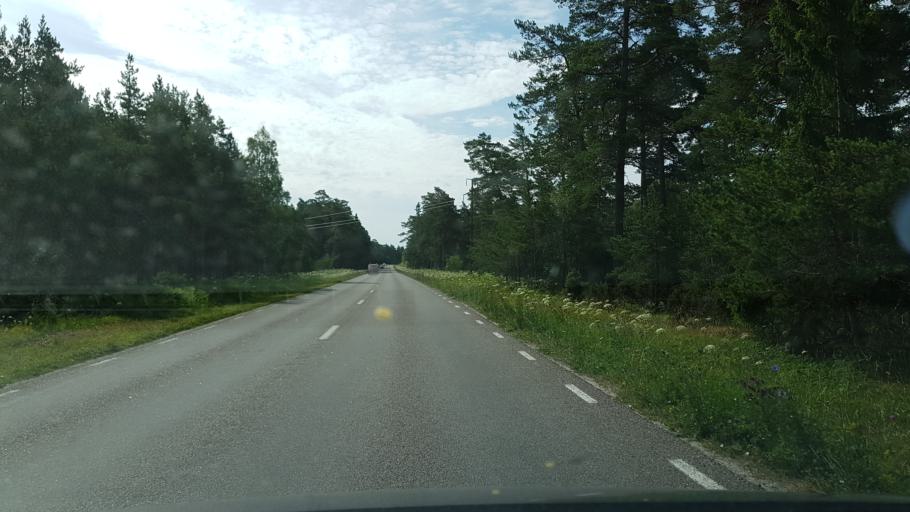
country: SE
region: Gotland
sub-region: Gotland
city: Hemse
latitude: 57.4604
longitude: 18.5734
